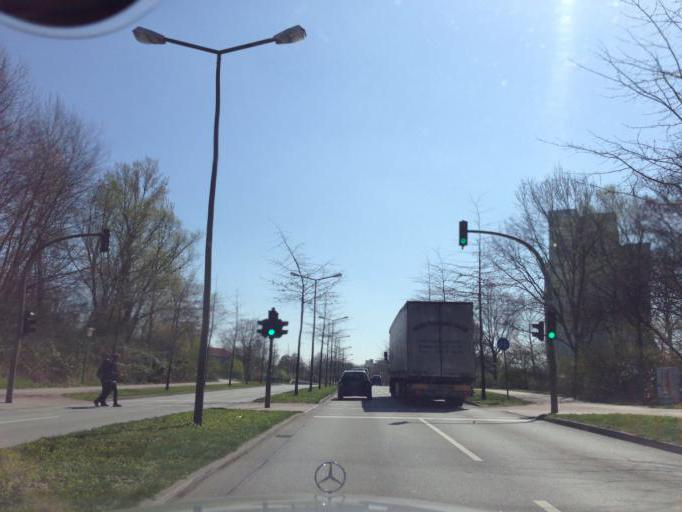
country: DE
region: Hamburg
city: Alsterdorf
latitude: 53.6098
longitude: 10.0245
